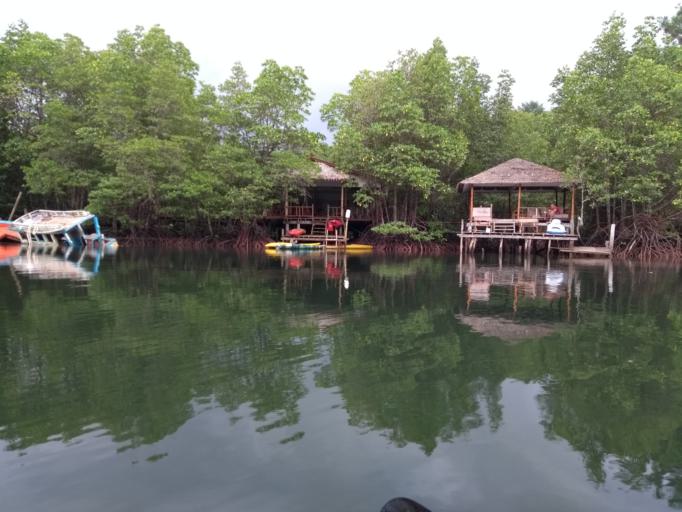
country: TH
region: Trat
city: Ko Kut
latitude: 11.6344
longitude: 102.5499
